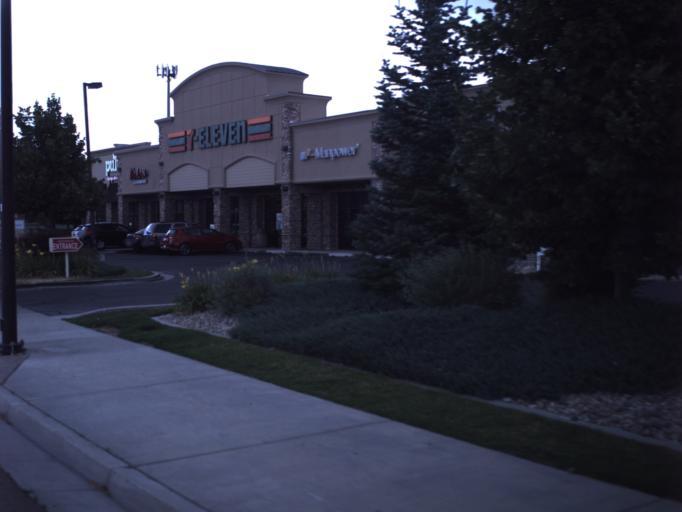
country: US
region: Utah
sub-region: Salt Lake County
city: Sandy City
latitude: 40.5756
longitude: -111.8907
